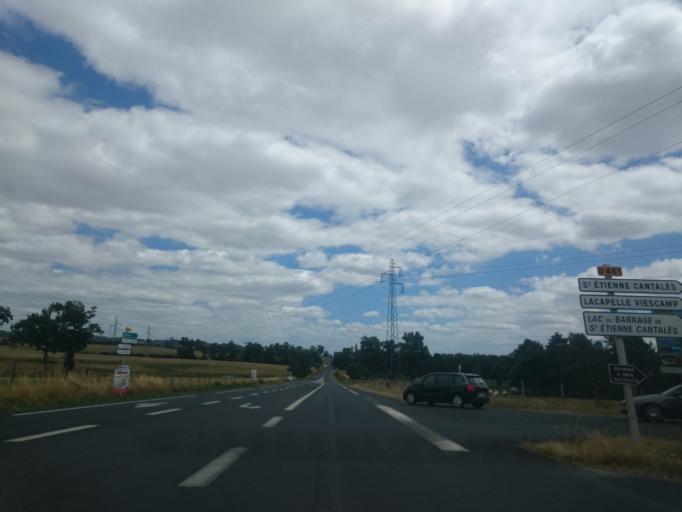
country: FR
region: Auvergne
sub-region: Departement du Cantal
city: Saint-Paul-des-Landes
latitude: 44.9549
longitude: 2.2802
